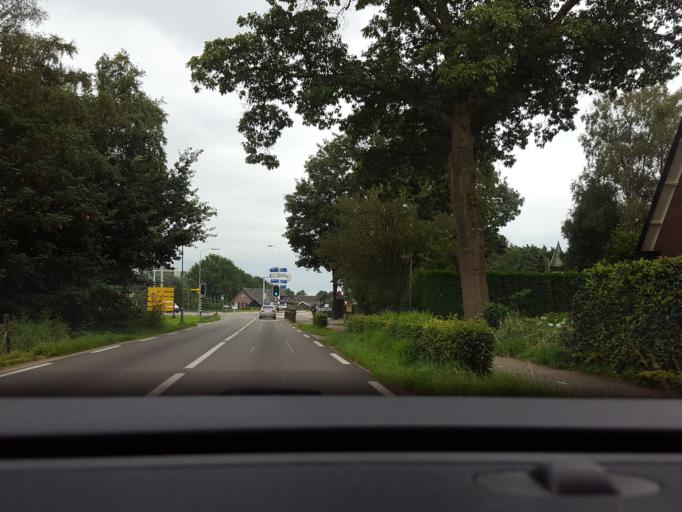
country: NL
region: Gelderland
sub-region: Gemeente Brummen
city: Eerbeek
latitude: 52.0957
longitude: 6.0881
